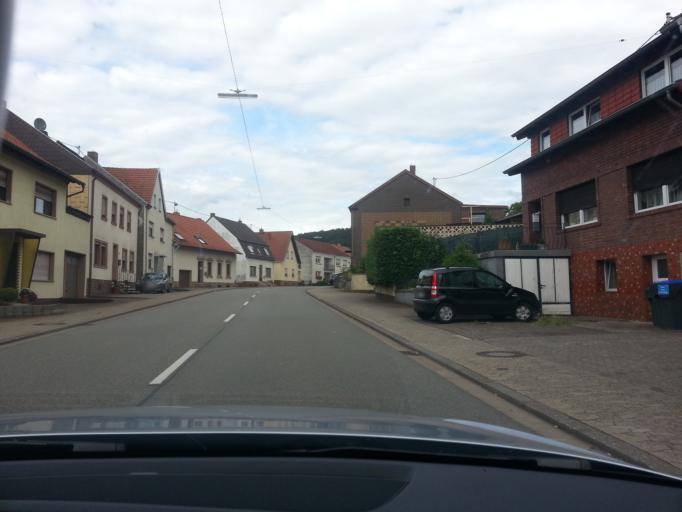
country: DE
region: Saarland
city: Eppelborn
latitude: 49.4101
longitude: 6.9743
